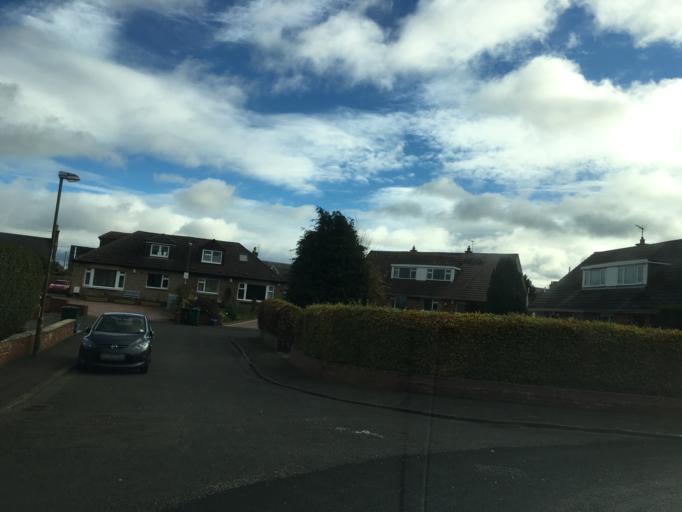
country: GB
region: Scotland
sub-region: Midlothian
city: Loanhead
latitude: 55.9136
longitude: -3.1701
